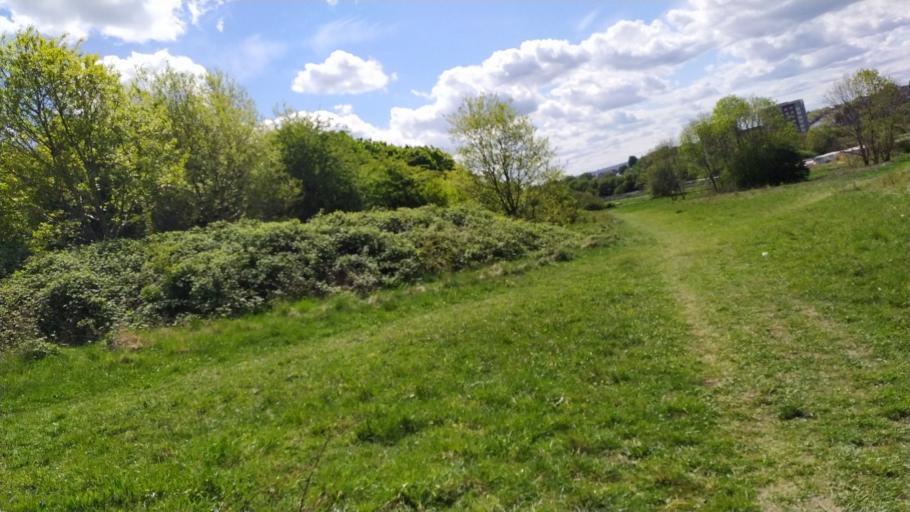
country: GB
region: England
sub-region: City and Borough of Leeds
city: Shadwell
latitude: 53.8090
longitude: -1.4825
